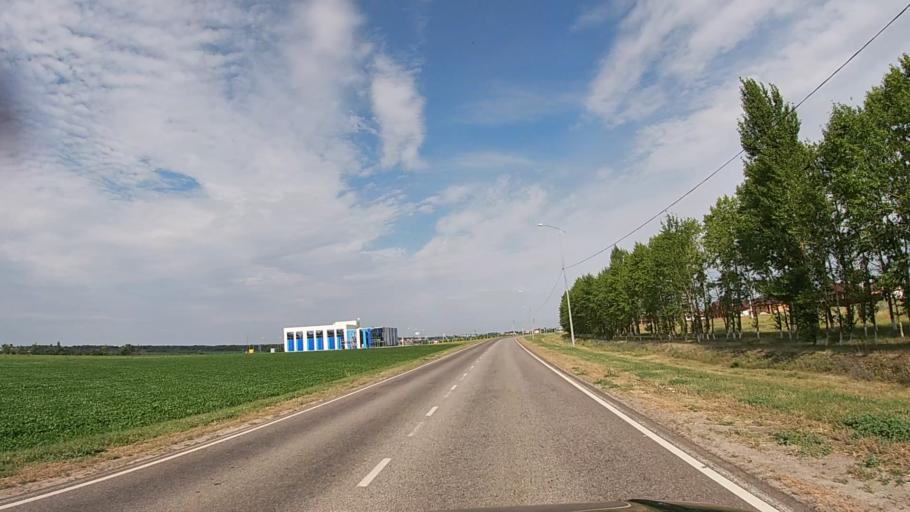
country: RU
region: Belgorod
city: Krasnaya Yaruga
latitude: 50.7962
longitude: 35.6951
